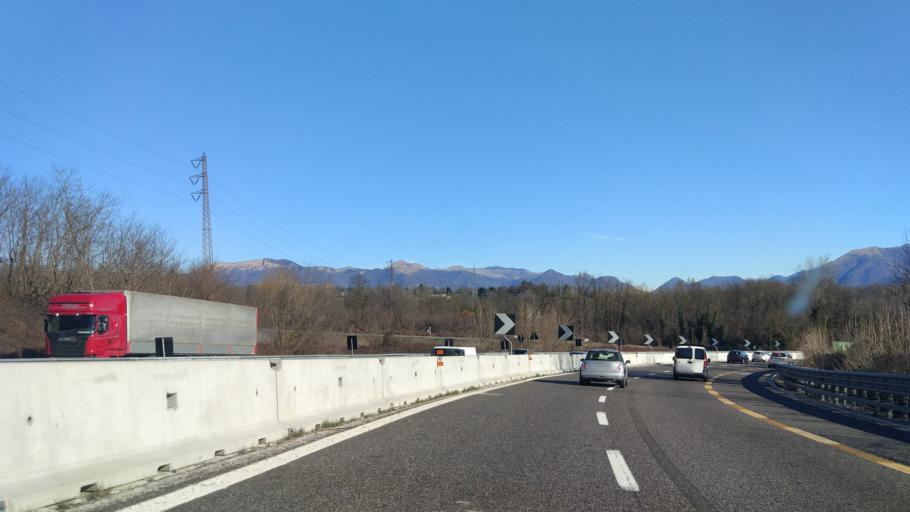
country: IT
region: Lombardy
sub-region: Provincia di Monza e Brianza
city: Briosco
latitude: 45.7139
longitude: 9.2274
